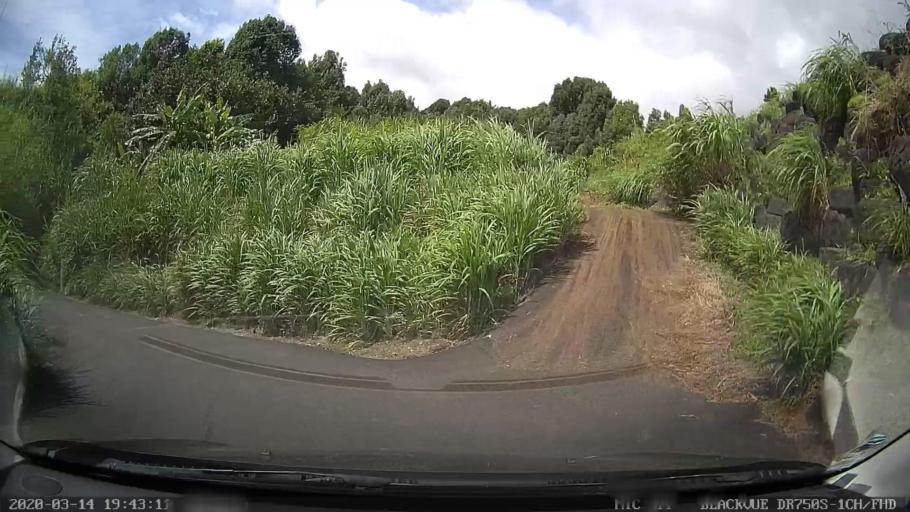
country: RE
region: Reunion
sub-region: Reunion
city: Sainte-Marie
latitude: -20.9479
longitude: 55.5272
